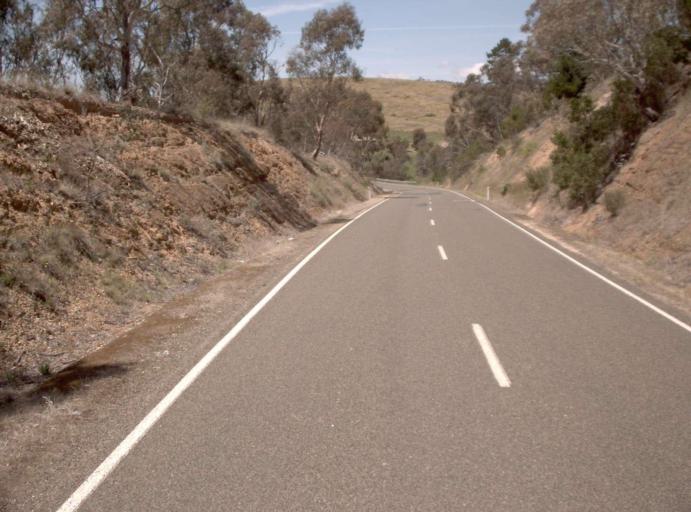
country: AU
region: Victoria
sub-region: Alpine
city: Mount Beauty
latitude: -37.1043
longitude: 147.6025
